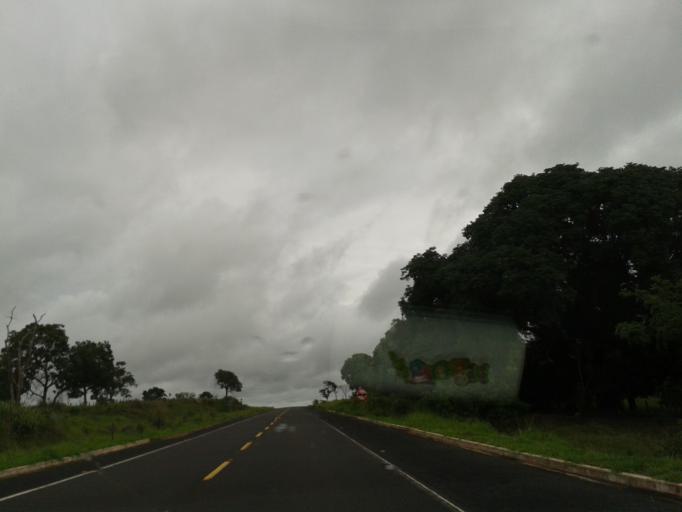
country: BR
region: Minas Gerais
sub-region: Santa Vitoria
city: Santa Vitoria
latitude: -19.2296
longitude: -50.0185
